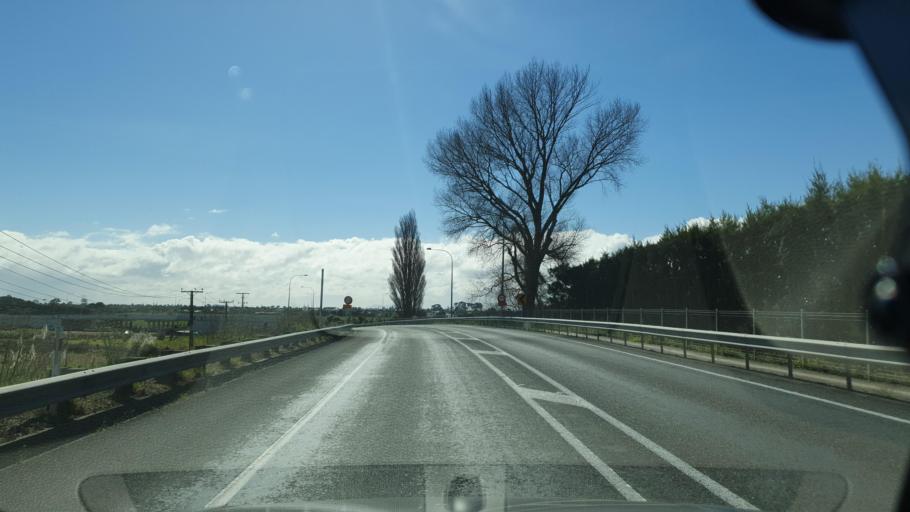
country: NZ
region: Bay of Plenty
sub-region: Tauranga City
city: Tauranga
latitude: -37.7182
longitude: 176.2844
